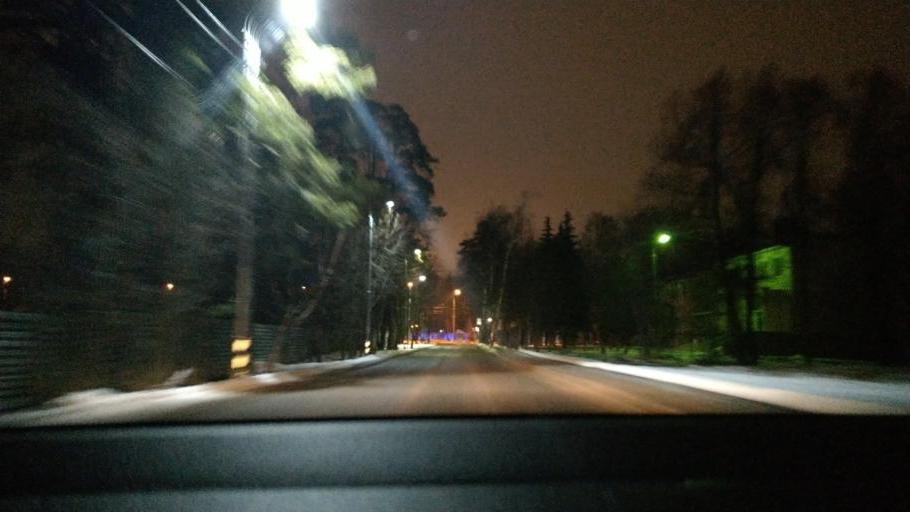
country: RU
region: Moskovskaya
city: Barvikha
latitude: 55.7209
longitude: 37.2741
